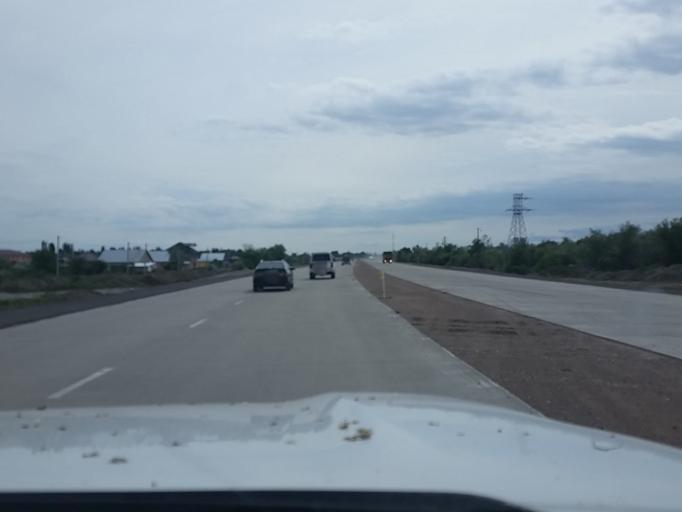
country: KZ
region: Almaty Oblysy
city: Turgen'
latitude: 43.5834
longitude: 78.2182
